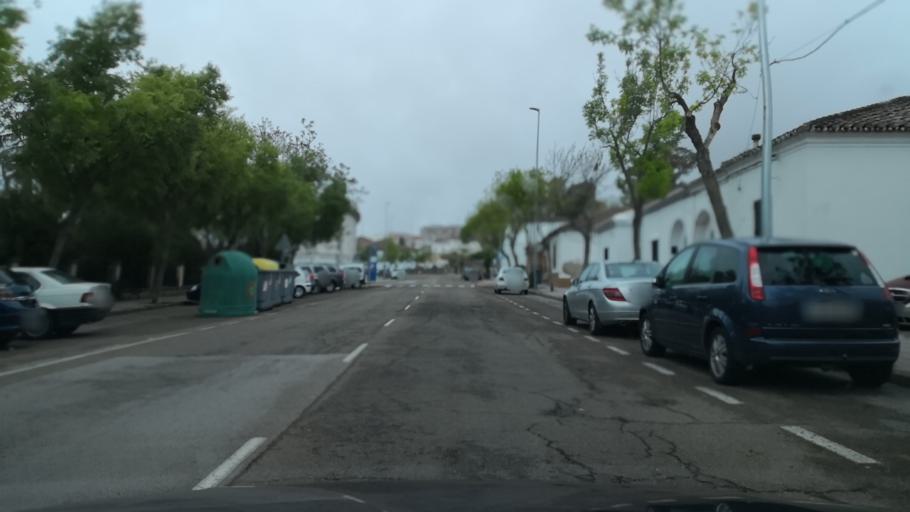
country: ES
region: Extremadura
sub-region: Provincia de Caceres
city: Caceres
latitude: 39.4809
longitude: -6.3682
